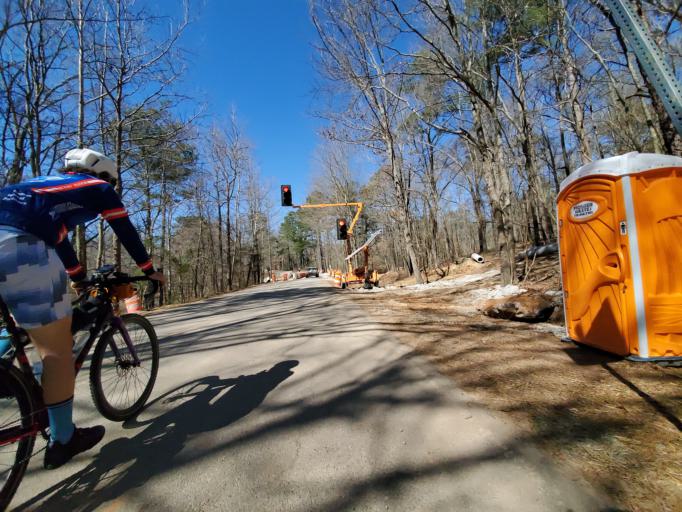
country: US
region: Georgia
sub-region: Barrow County
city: Winder
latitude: 33.9831
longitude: -83.7305
